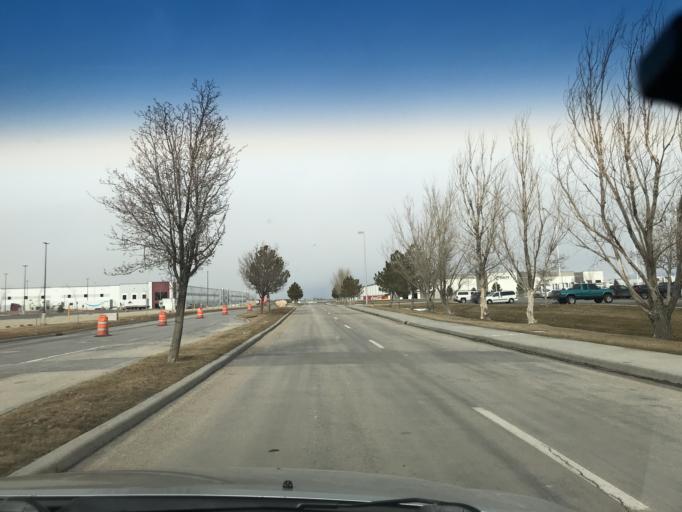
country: US
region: Utah
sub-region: Salt Lake County
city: West Valley City
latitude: 40.7852
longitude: -112.0250
